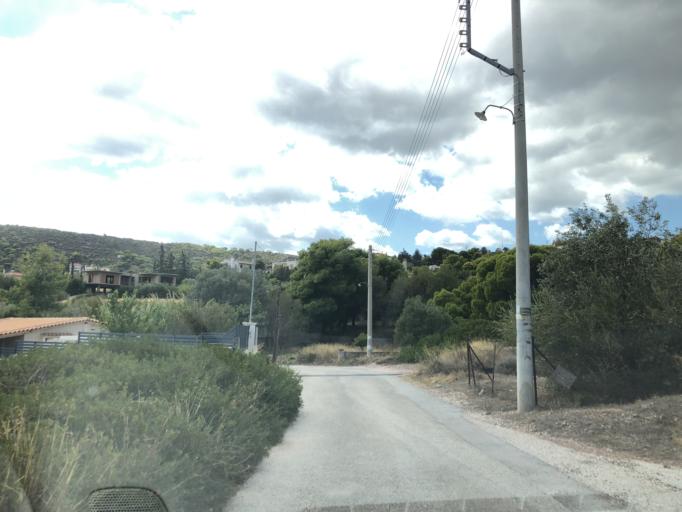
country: GR
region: Attica
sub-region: Nomarchia Anatolikis Attikis
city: Agios Dimitrios Kropias
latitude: 37.8156
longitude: 23.8668
